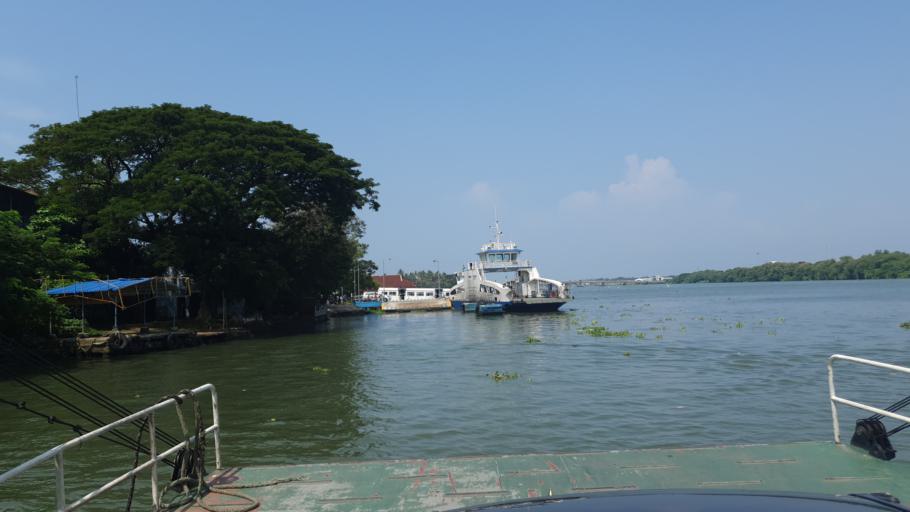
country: IN
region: Kerala
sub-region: Ernakulam
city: Cochin
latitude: 9.9729
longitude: 76.2448
